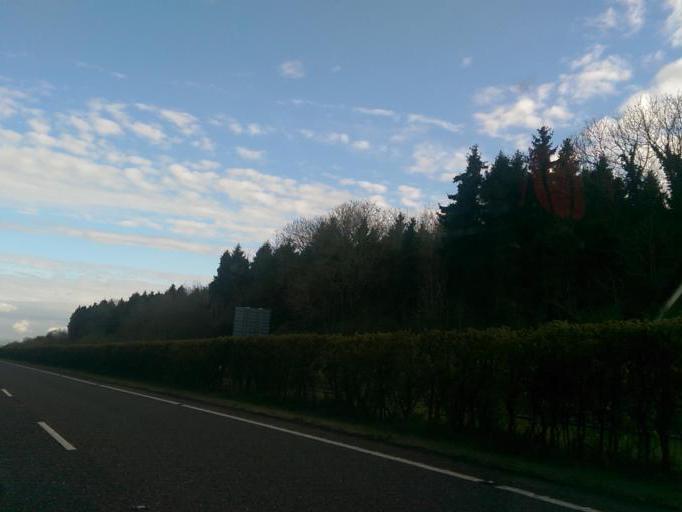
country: IE
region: Leinster
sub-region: Kildare
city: Kilcock
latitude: 53.3945
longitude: -6.6785
